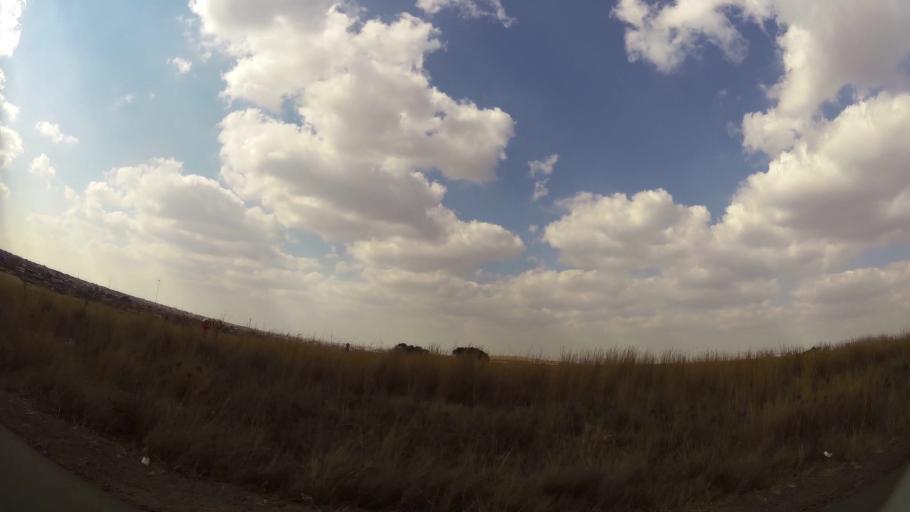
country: ZA
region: Mpumalanga
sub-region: Nkangala District Municipality
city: Delmas
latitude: -26.1094
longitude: 28.6787
